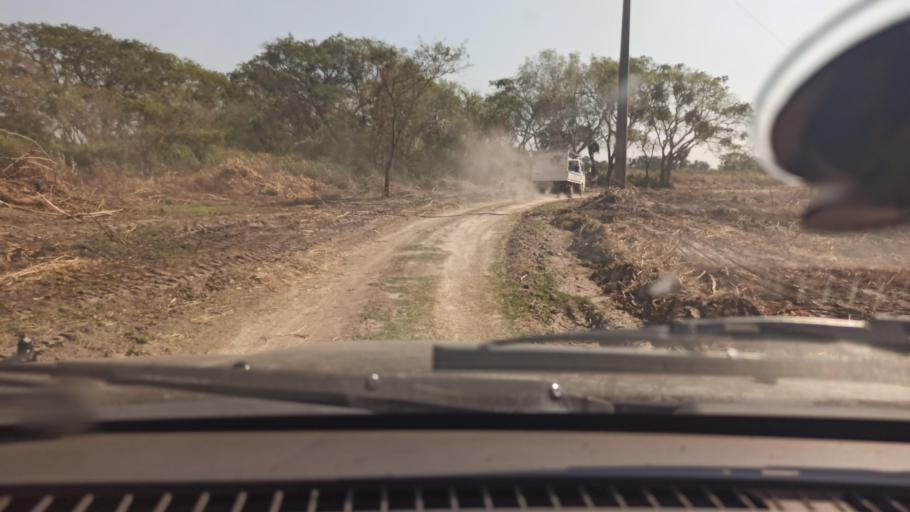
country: PY
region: Asuncion
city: Asuncion
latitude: -25.3426
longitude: -57.6765
